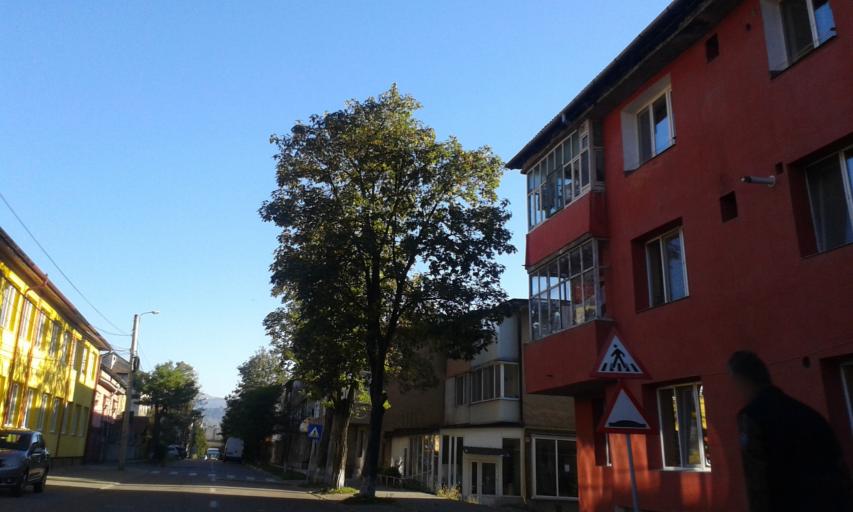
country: RO
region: Hunedoara
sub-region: Municipiul Petrosani
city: Petrosani
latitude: 45.4239
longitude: 23.3698
